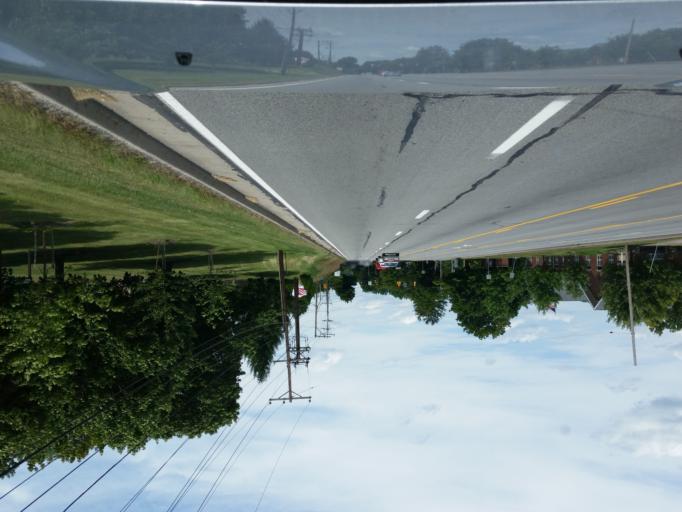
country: US
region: Pennsylvania
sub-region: Blair County
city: Lakemont
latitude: 40.4900
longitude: -78.3979
